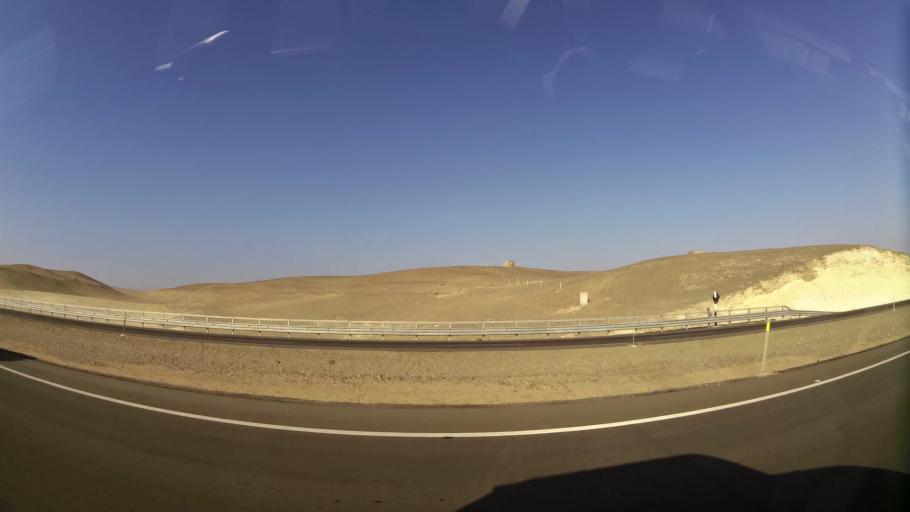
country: PE
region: Ica
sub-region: Provincia de Pisco
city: San Clemente
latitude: -13.6553
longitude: -76.1739
